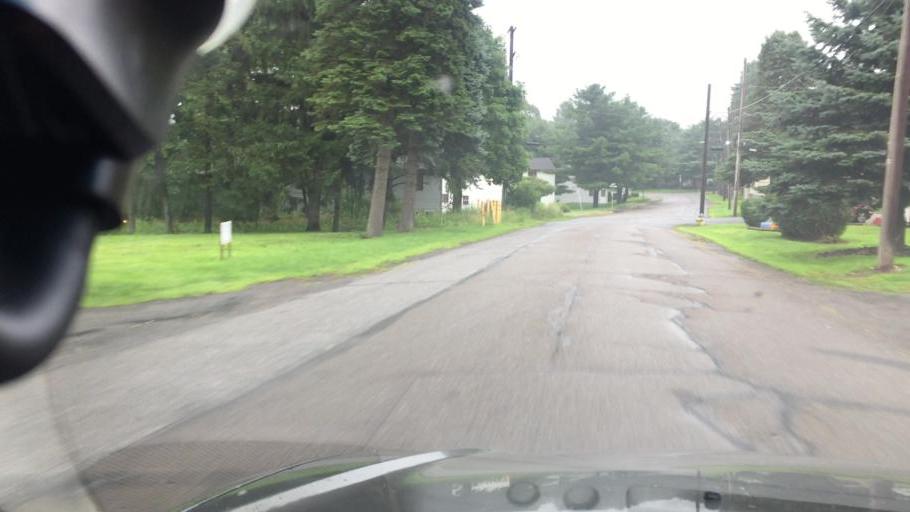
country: US
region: Pennsylvania
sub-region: Luzerne County
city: Freeland
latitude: 41.0245
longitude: -75.8983
